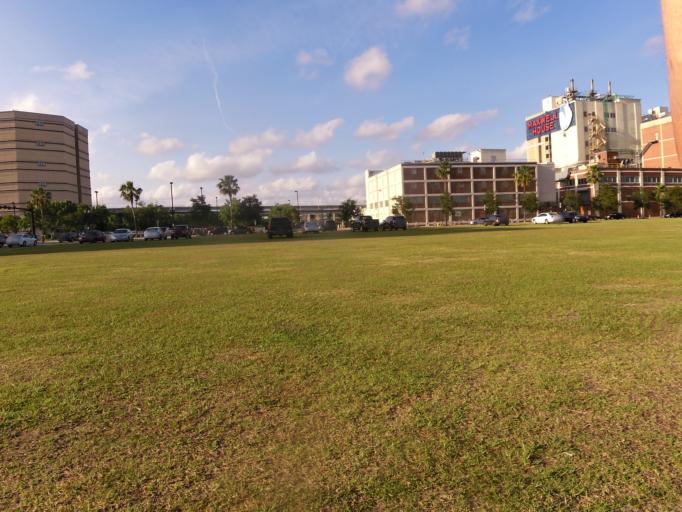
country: US
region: Florida
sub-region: Duval County
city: Jacksonville
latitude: 30.3237
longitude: -81.6497
